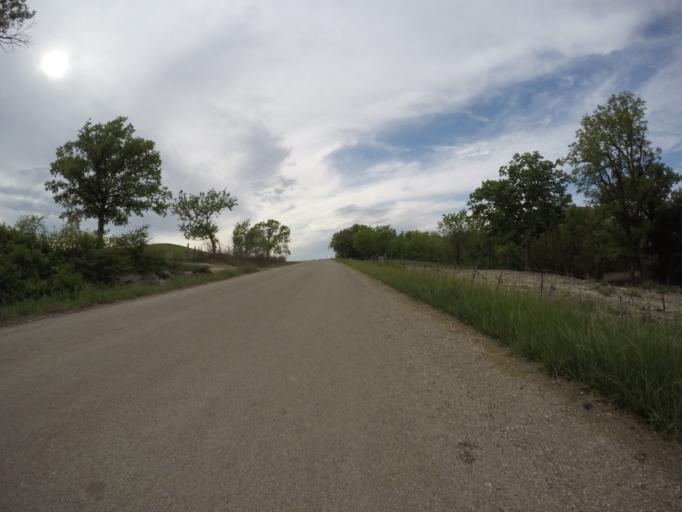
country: US
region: Kansas
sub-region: Riley County
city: Ogden
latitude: 39.0290
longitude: -96.6125
